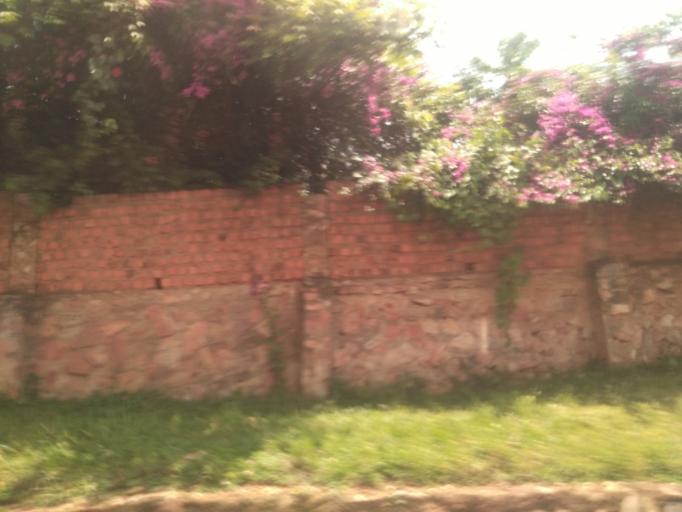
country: UG
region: Central Region
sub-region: Wakiso District
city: Entebbe
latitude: 0.0567
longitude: 32.4790
